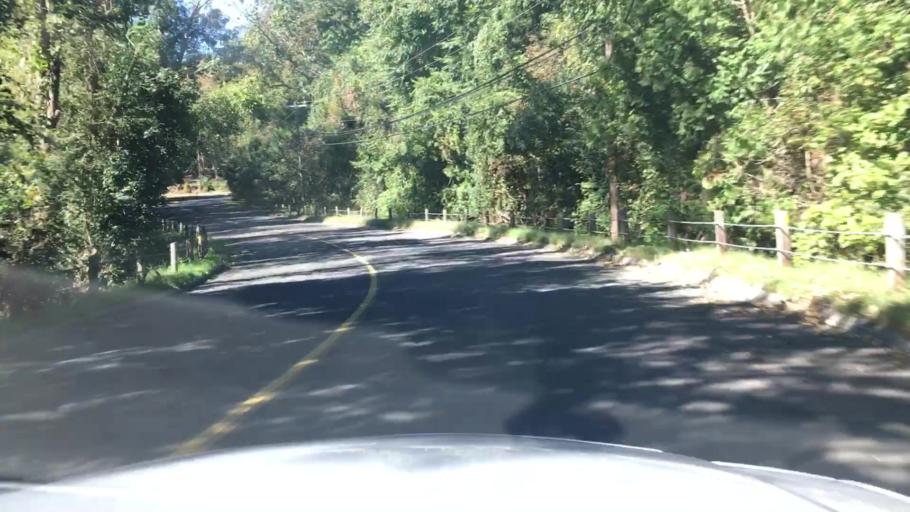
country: US
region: Connecticut
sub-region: Middlesex County
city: Essex Village
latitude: 41.3554
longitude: -72.4083
